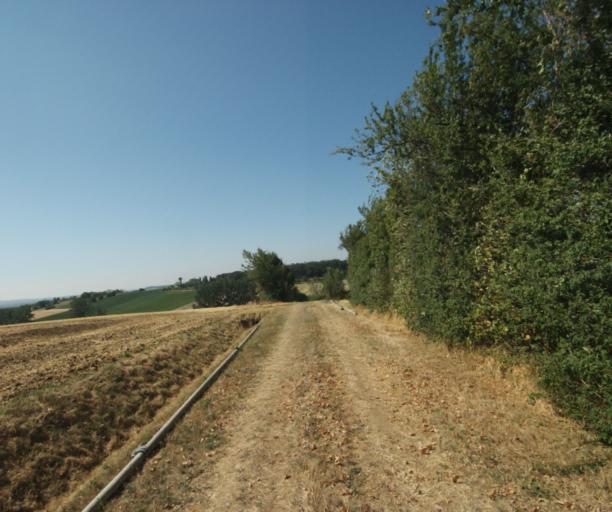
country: FR
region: Midi-Pyrenees
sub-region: Departement de la Haute-Garonne
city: Saint-Felix-Lauragais
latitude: 43.5029
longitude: 1.9280
